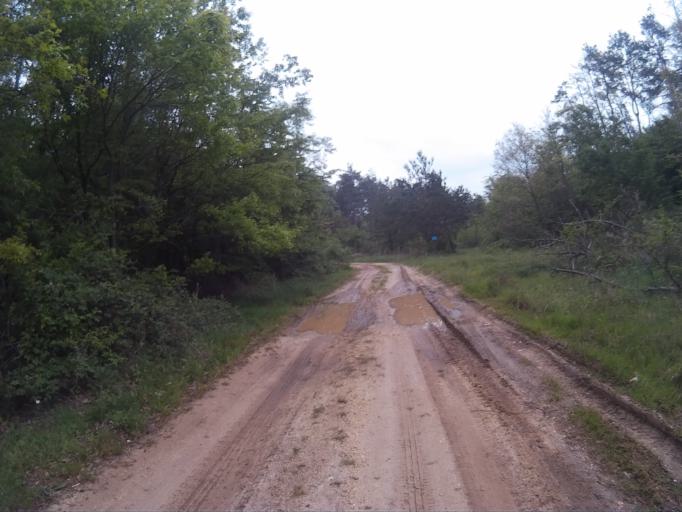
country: HU
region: Vas
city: Vasvar
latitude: 47.0488
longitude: 16.8430
